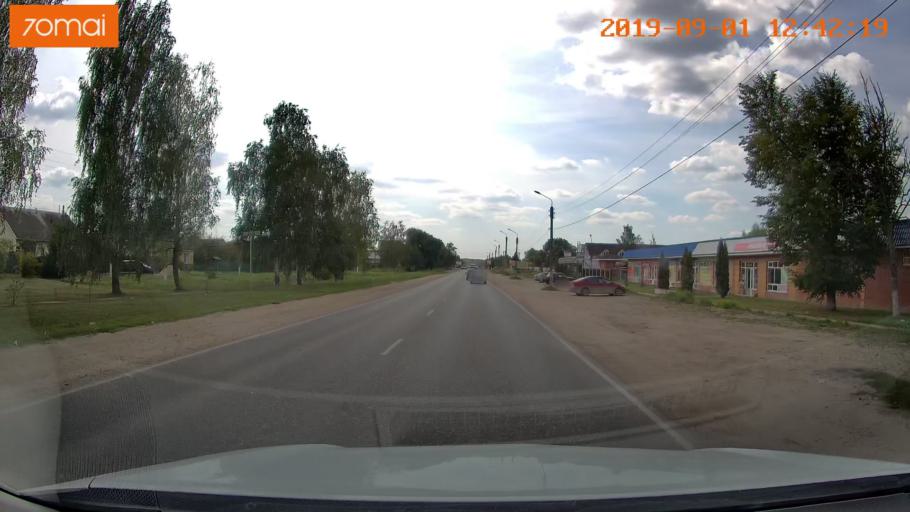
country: RU
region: Kaluga
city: Maloyaroslavets
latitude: 55.0016
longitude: 36.4406
